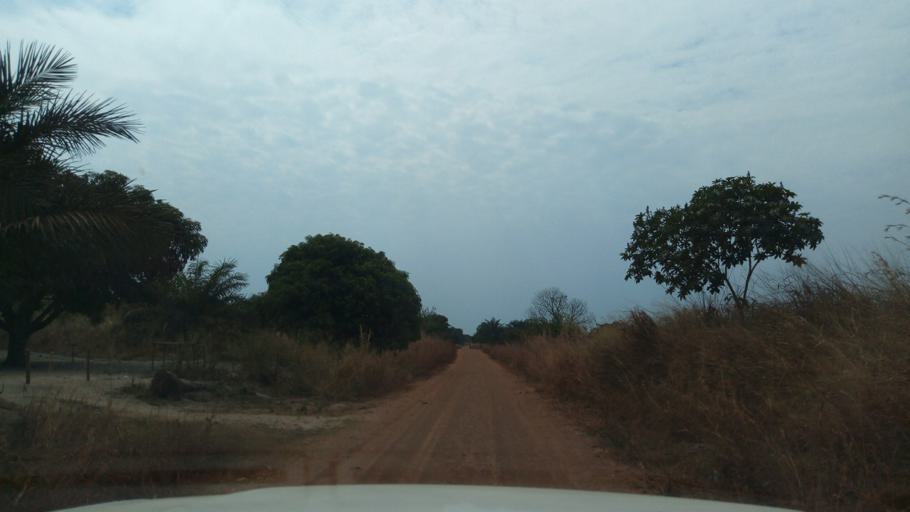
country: ZM
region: Northern
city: Kaputa
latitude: -8.3734
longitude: 28.9636
